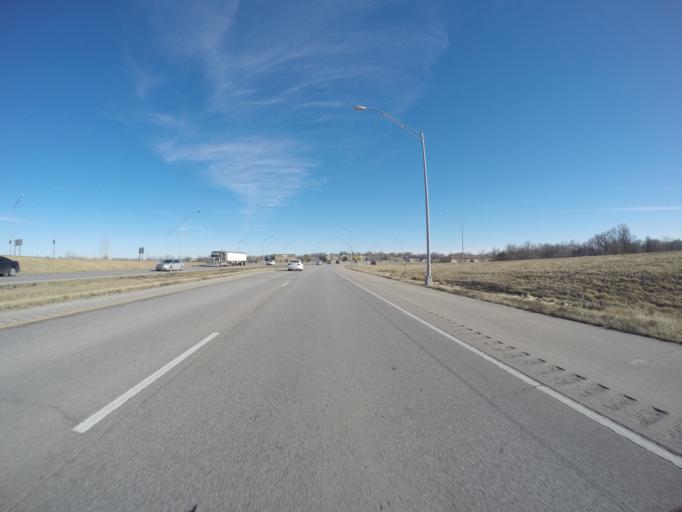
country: US
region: Nebraska
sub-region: Lancaster County
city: Lincoln
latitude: 40.8021
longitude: -96.7429
